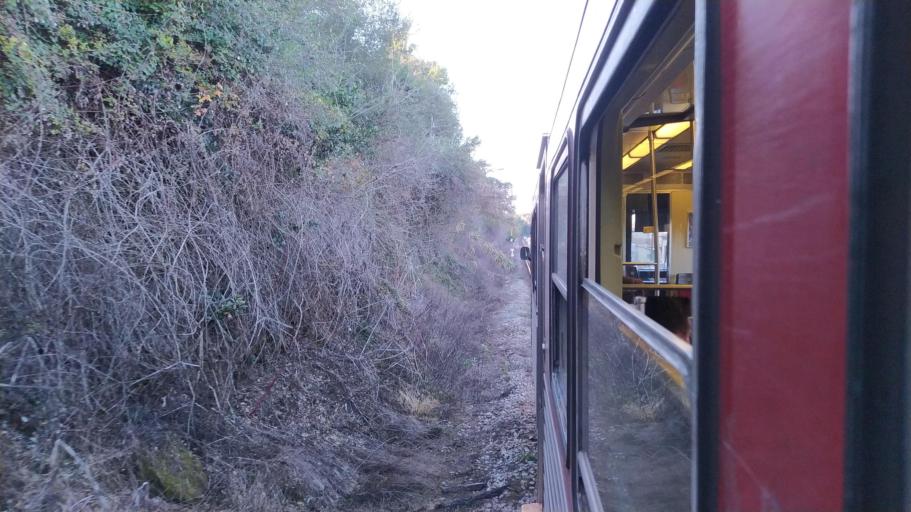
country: PT
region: Aveiro
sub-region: Aveiro
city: Eixo
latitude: 40.6103
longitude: -8.5324
